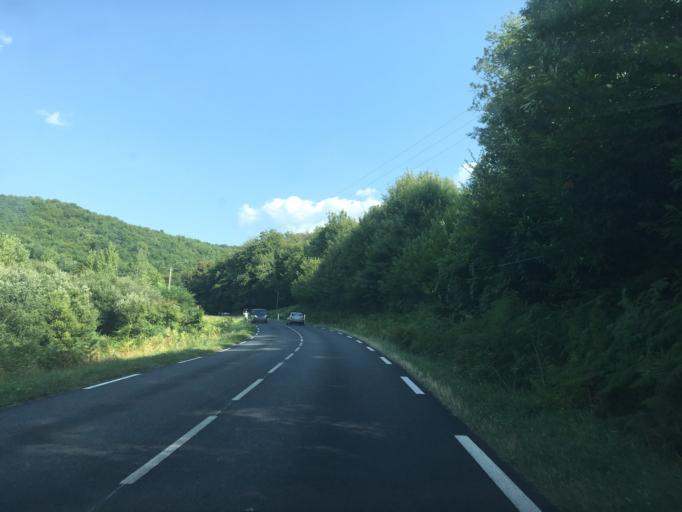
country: FR
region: Aquitaine
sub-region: Departement de la Dordogne
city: Sarlat-la-Caneda
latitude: 44.8505
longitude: 1.1870
